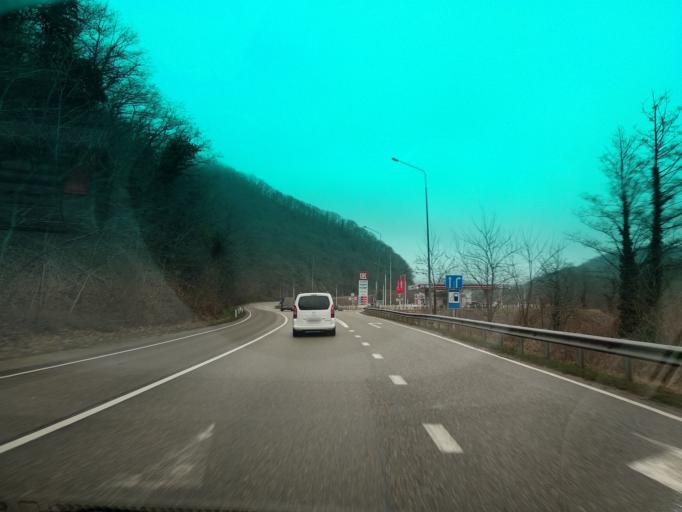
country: RU
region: Krasnodarskiy
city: Ol'ginka
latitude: 44.2160
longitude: 38.8947
